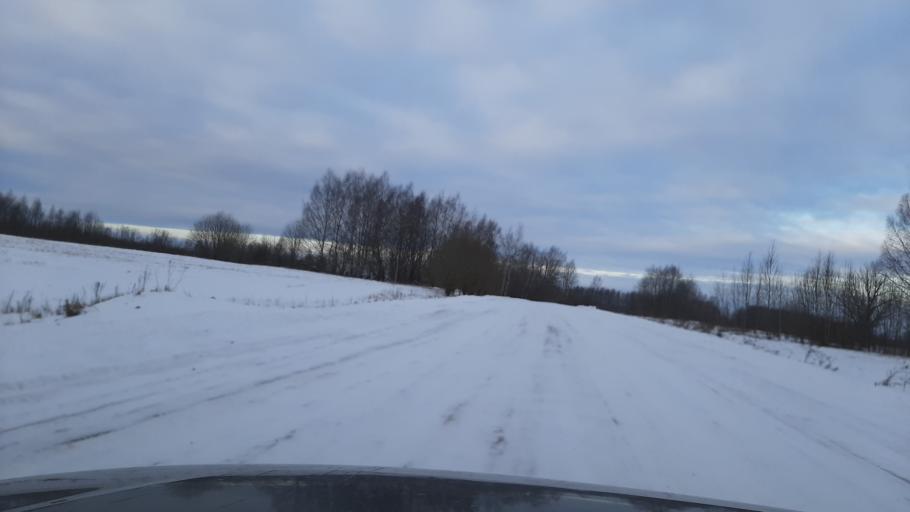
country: RU
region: Kostroma
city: Kosmynino
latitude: 57.4791
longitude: 40.8542
